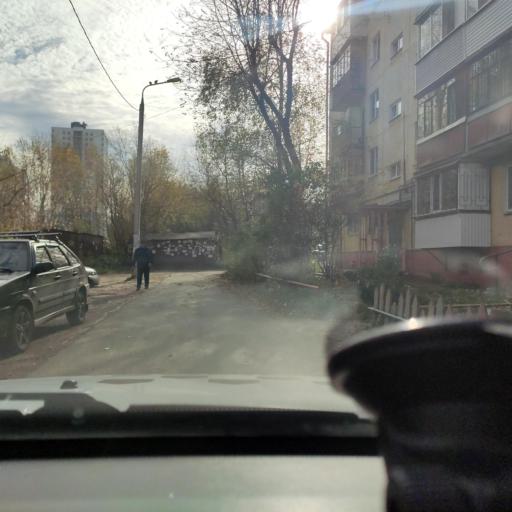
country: RU
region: Perm
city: Perm
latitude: 57.9993
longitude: 56.2164
